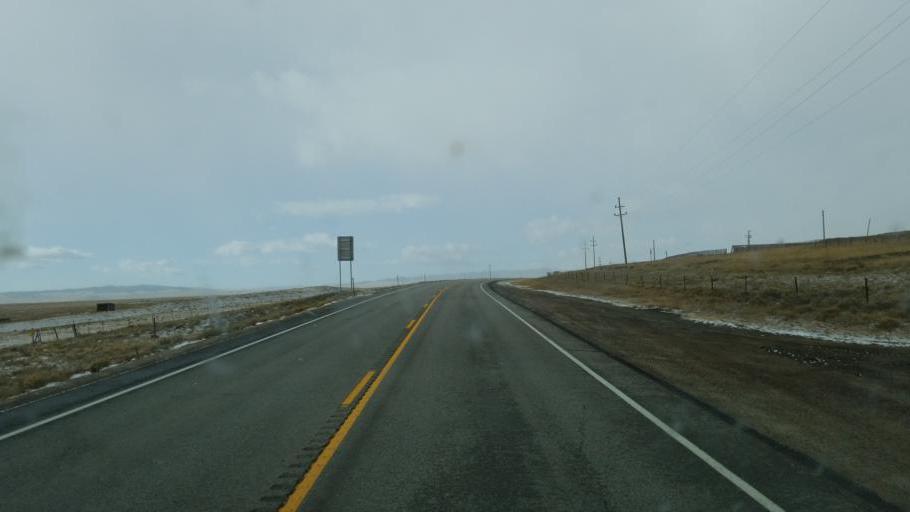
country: US
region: Colorado
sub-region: Summit County
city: Breckenridge
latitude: 39.3881
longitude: -105.7890
